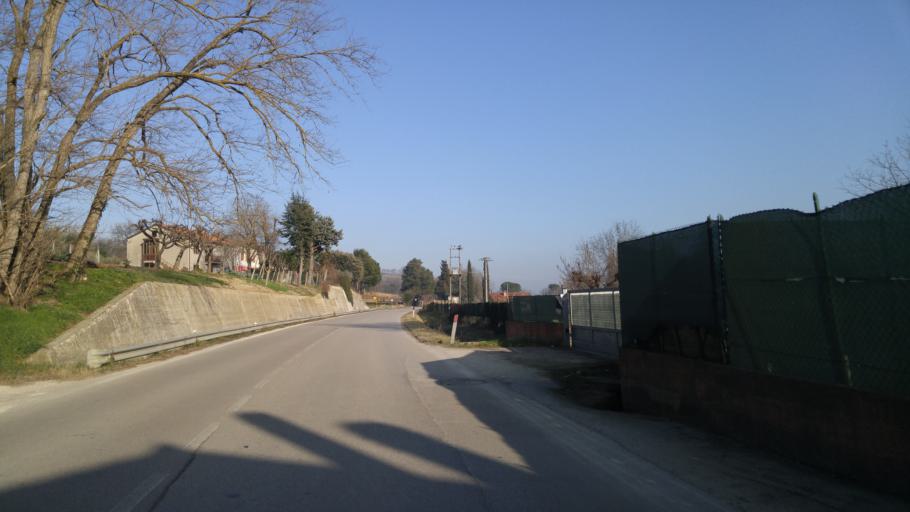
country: IT
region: The Marches
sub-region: Provincia di Pesaro e Urbino
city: Fenile
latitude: 43.8363
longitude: 12.9351
